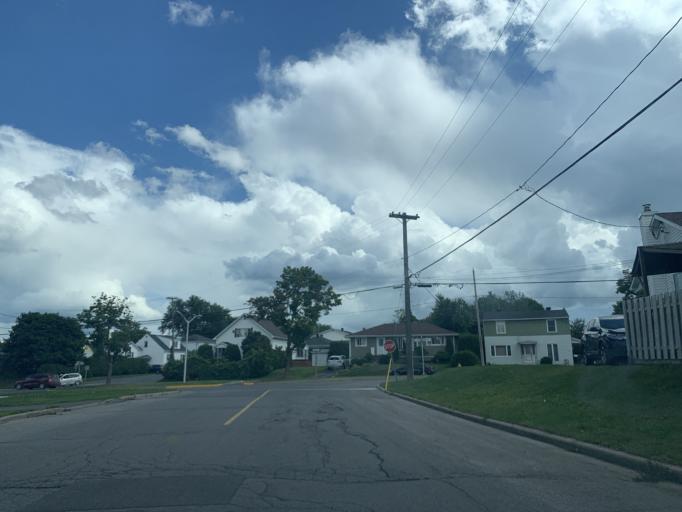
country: CA
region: Ontario
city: Hawkesbury
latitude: 45.6056
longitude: -74.6072
